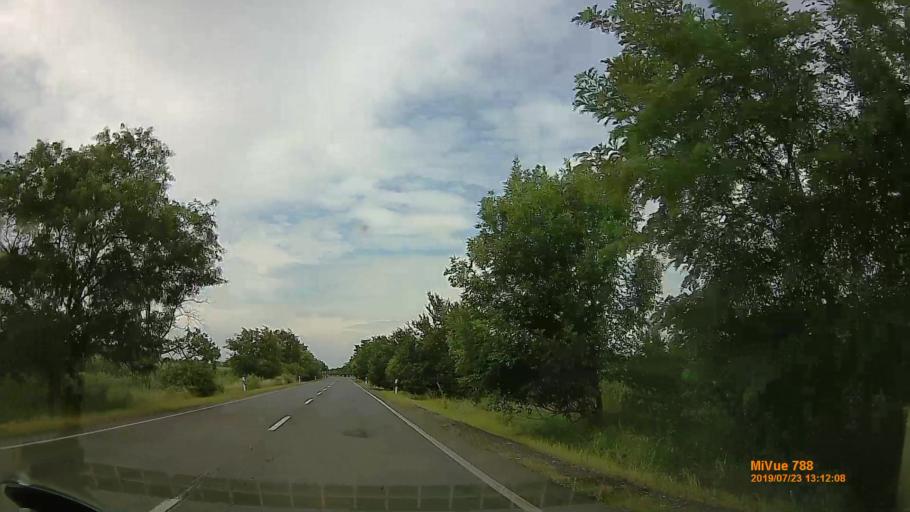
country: HU
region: Szabolcs-Szatmar-Bereg
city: Tiszavasvari
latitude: 47.9300
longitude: 21.2574
